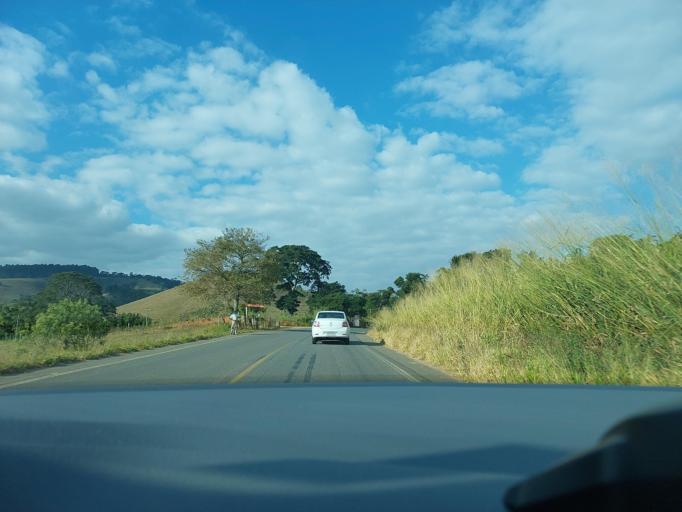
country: BR
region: Minas Gerais
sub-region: Vicosa
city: Vicosa
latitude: -20.8264
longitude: -42.7721
